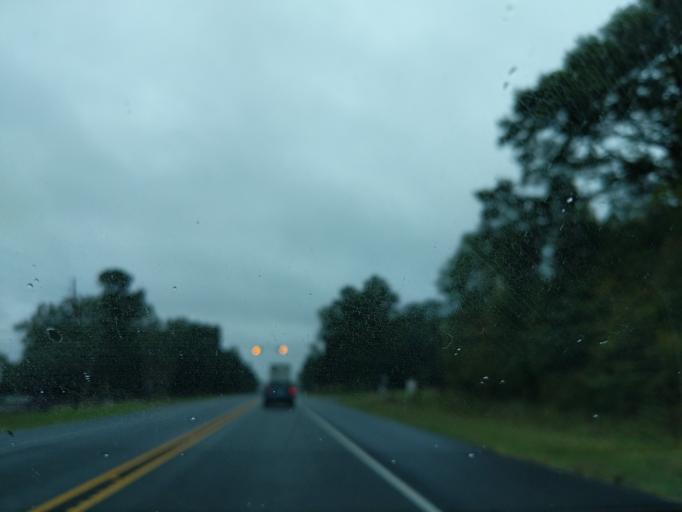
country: US
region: Louisiana
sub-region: Caddo Parish
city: Greenwood
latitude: 32.4277
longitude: -93.9848
